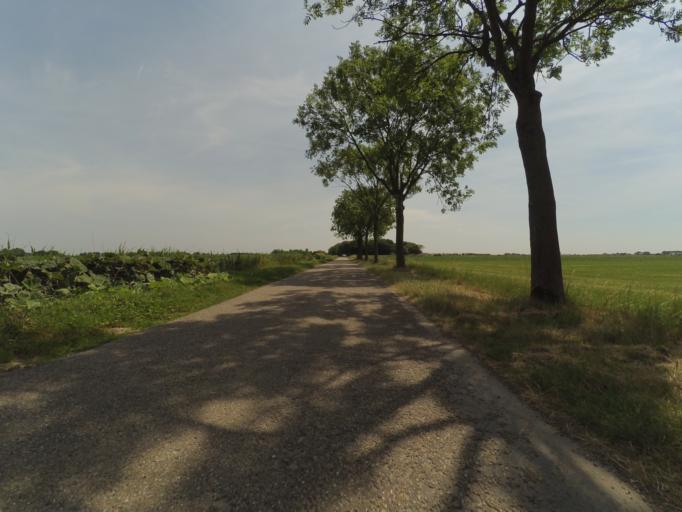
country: NL
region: North Brabant
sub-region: Gemeente Steenbergen
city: Kruisland
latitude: 51.5553
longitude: 4.3947
